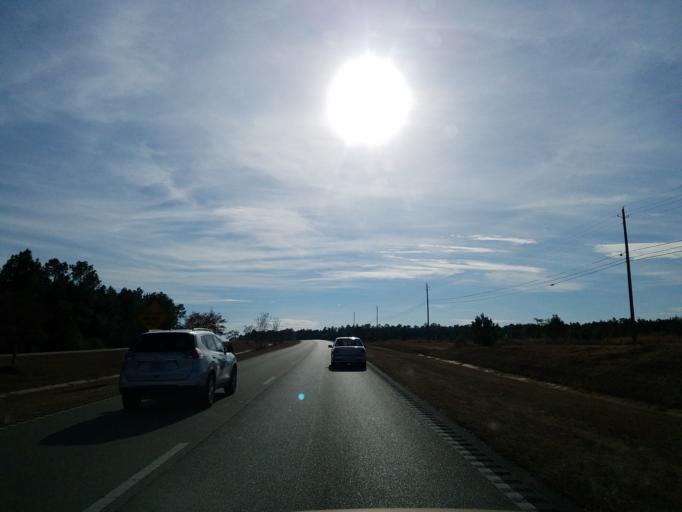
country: US
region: Mississippi
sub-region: Lamar County
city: West Hattiesburg
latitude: 31.2671
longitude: -89.3342
